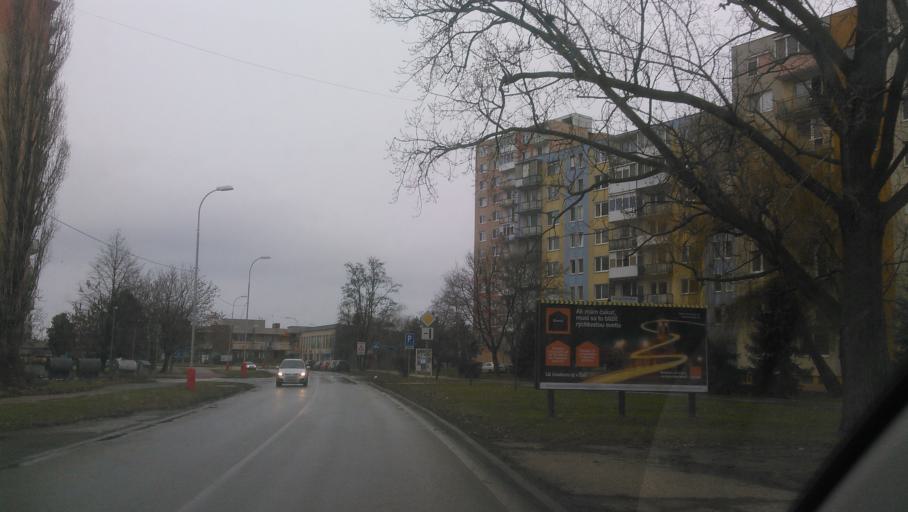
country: SK
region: Nitriansky
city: Sellye
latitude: 48.1503
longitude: 17.8688
